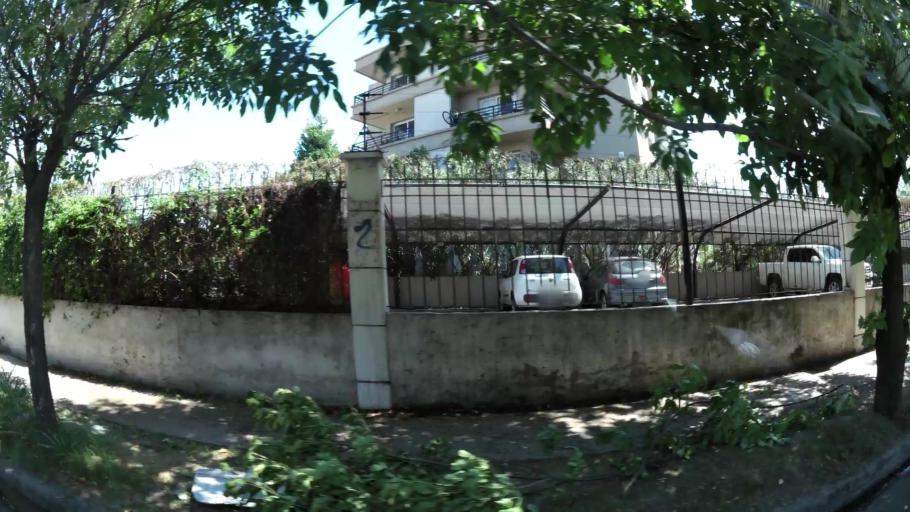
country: AR
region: Cordoba
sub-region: Departamento de Capital
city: Cordoba
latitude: -31.4568
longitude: -64.1627
